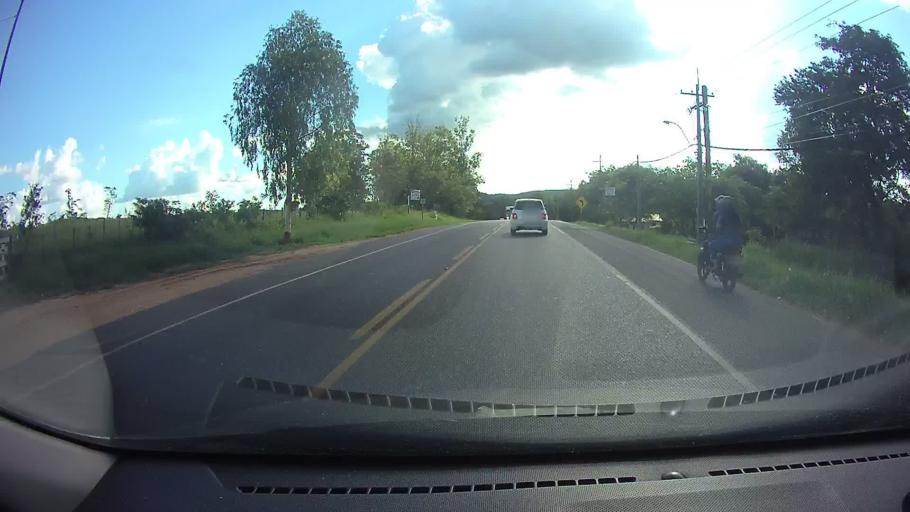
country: PY
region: Cordillera
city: Caacupe
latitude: -25.3852
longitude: -57.0552
